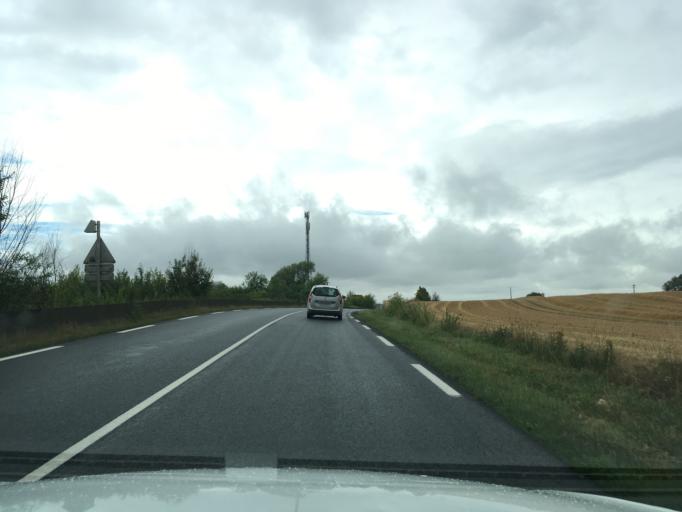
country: FR
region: Picardie
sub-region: Departement de l'Aisne
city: Origny-Sainte-Benoite
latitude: 49.8389
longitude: 3.4674
